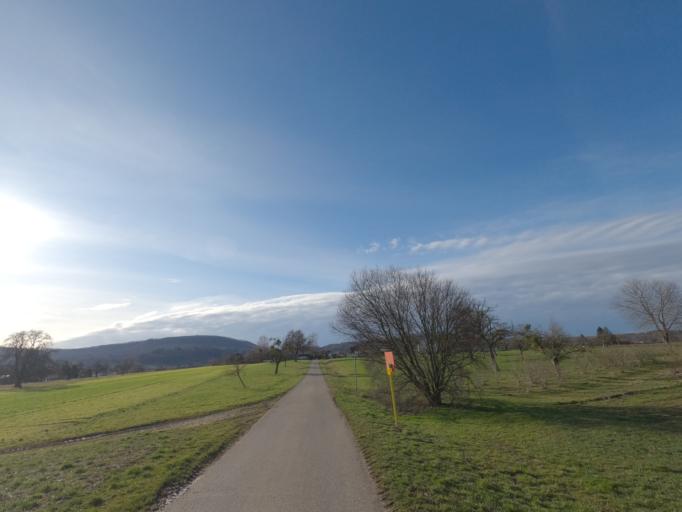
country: DE
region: Baden-Wuerttemberg
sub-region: Regierungsbezirk Stuttgart
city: Boll
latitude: 48.6502
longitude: 9.6076
